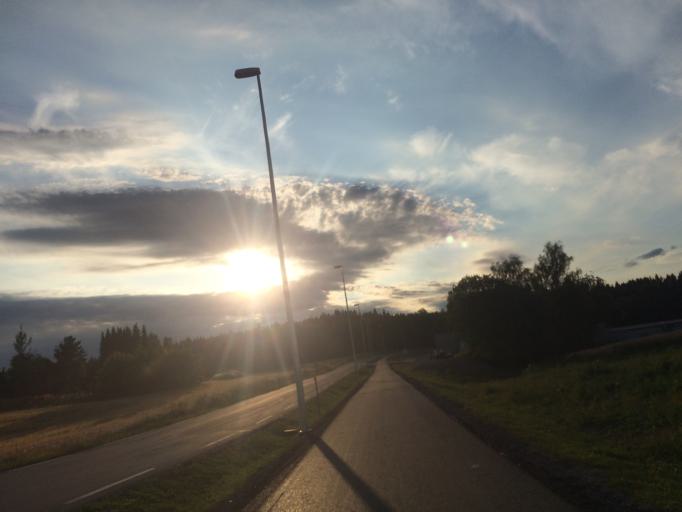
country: NO
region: Akershus
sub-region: Ski
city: Ski
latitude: 59.6966
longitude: 10.8541
